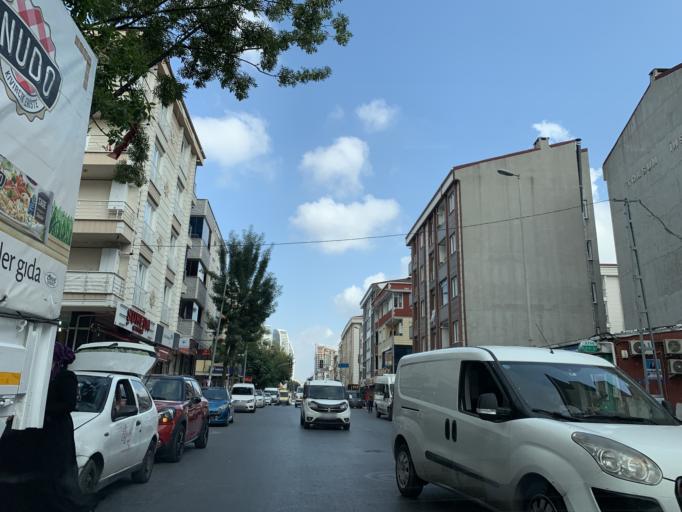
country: TR
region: Istanbul
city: Esenyurt
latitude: 41.0244
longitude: 28.6705
